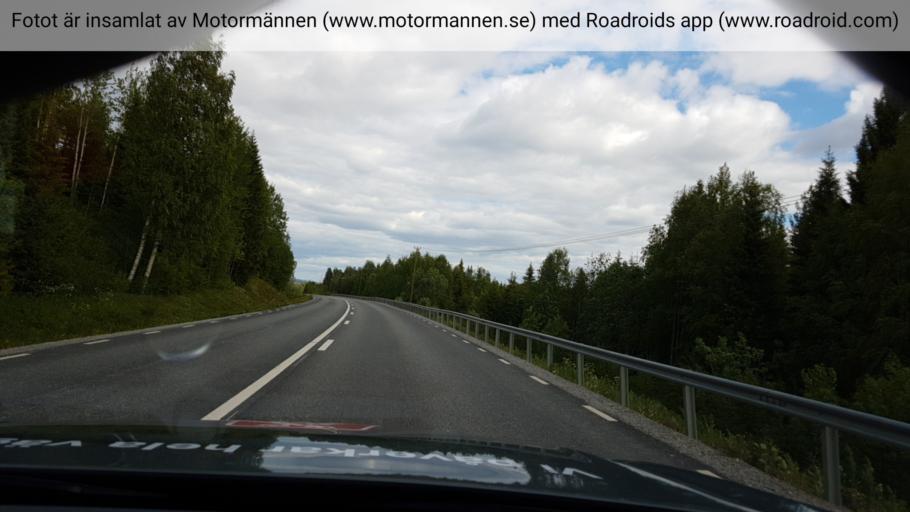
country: SE
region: Jaemtland
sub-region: Stroemsunds Kommun
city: Stroemsund
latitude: 64.1983
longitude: 15.6068
